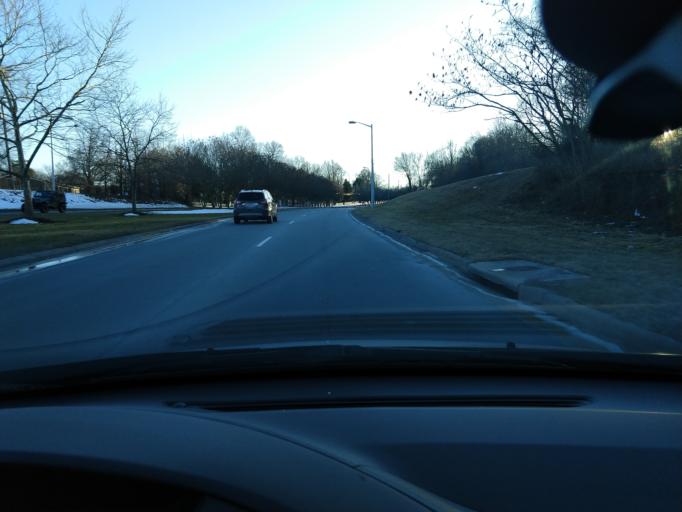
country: US
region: North Carolina
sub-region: Guilford County
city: Greensboro
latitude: 36.0556
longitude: -79.8037
